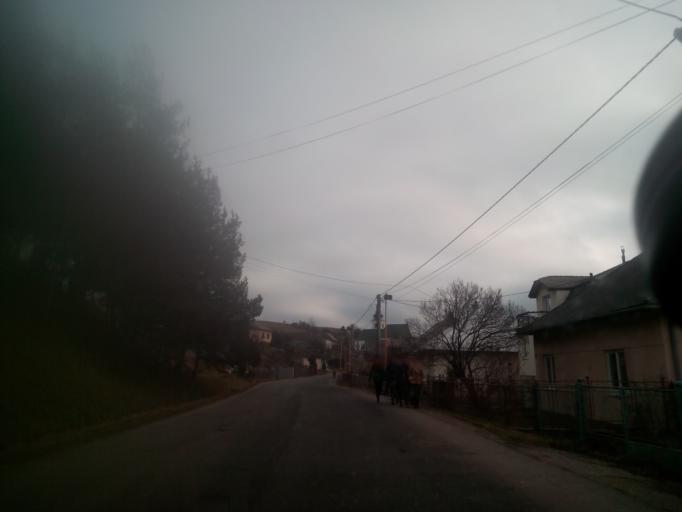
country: SK
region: Kosicky
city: Krompachy
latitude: 48.9232
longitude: 20.9344
